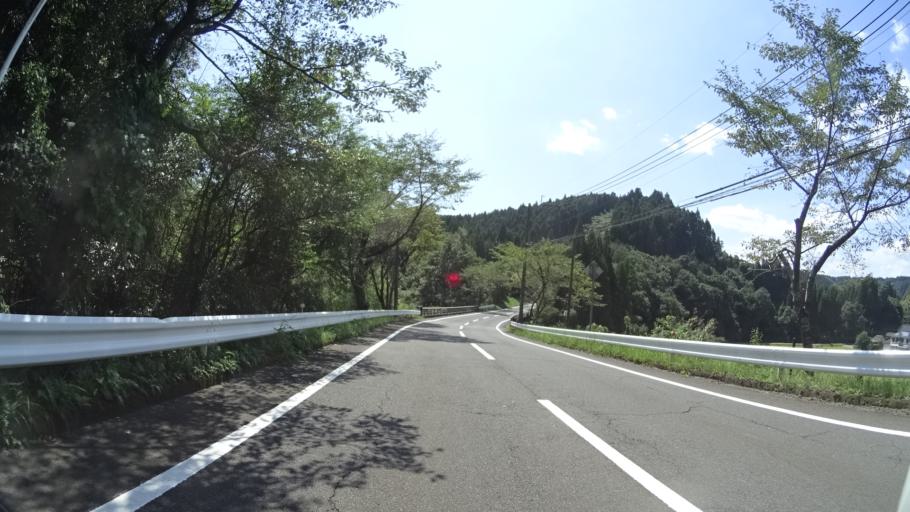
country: JP
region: Kagoshima
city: Kokubu-matsuki
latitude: 31.8269
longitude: 130.7292
